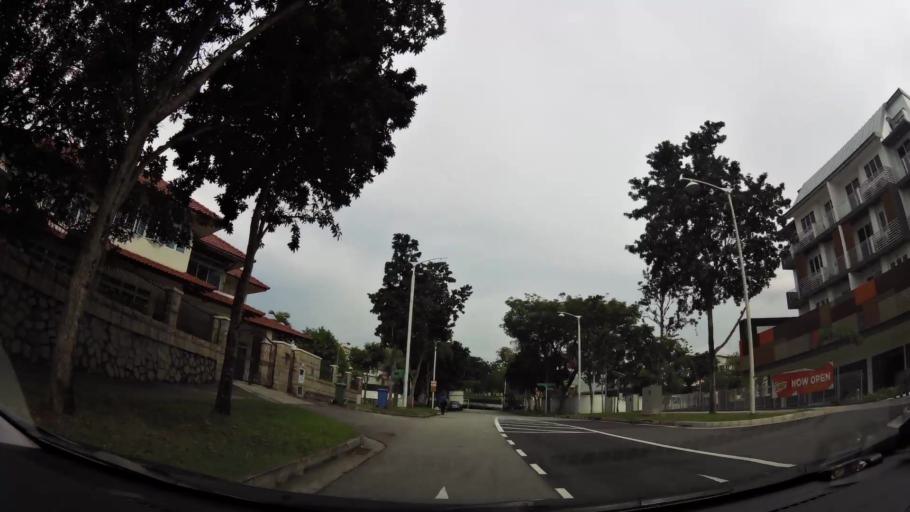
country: SG
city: Singapore
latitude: 1.3462
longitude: 103.8832
